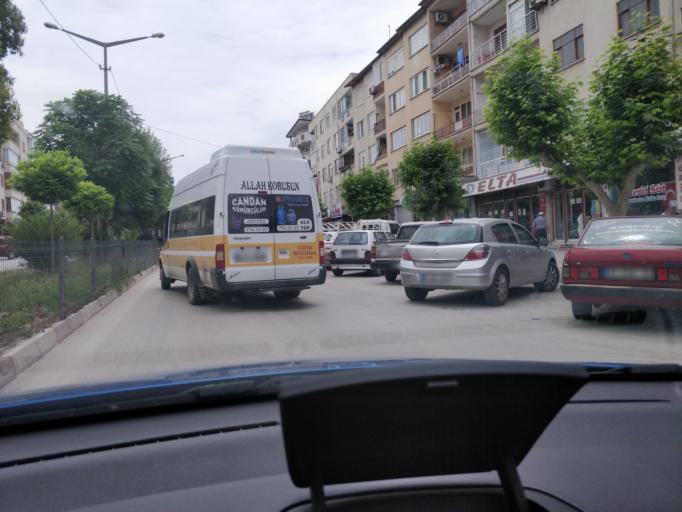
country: TR
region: Mersin
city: Mut
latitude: 36.6439
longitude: 33.4390
